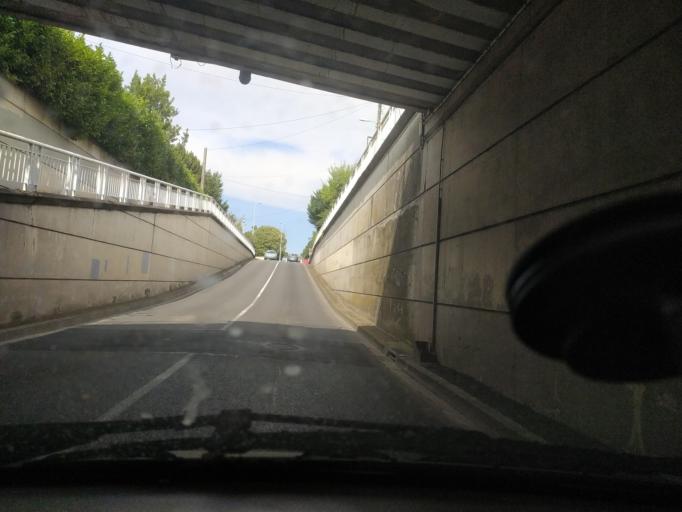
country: FR
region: Midi-Pyrenees
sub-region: Departement de la Haute-Garonne
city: Colomiers
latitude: 43.6033
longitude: 1.3352
